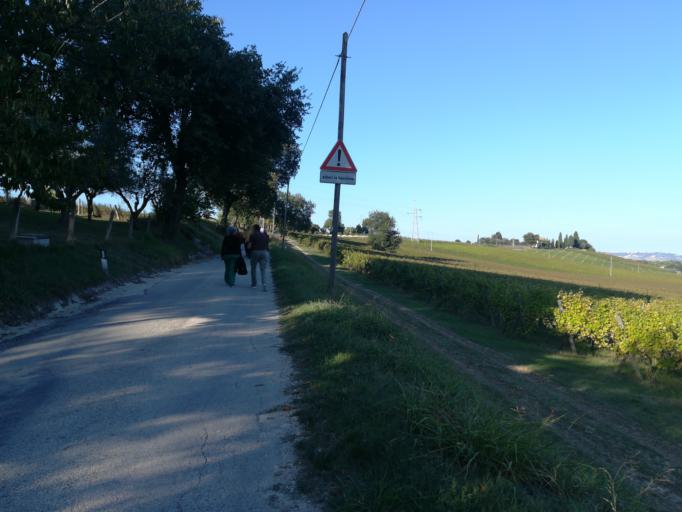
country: IT
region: The Marches
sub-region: Provincia di Macerata
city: Villa Potenza
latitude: 43.3316
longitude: 13.4157
